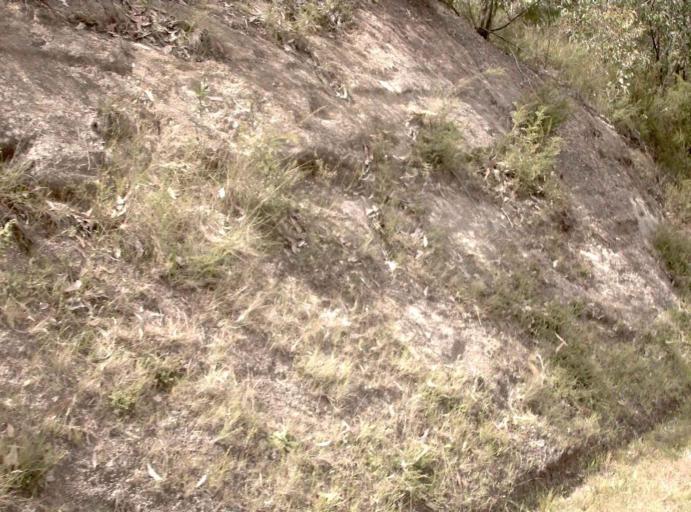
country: AU
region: Victoria
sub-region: Latrobe
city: Traralgon
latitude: -38.3153
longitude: 146.5709
